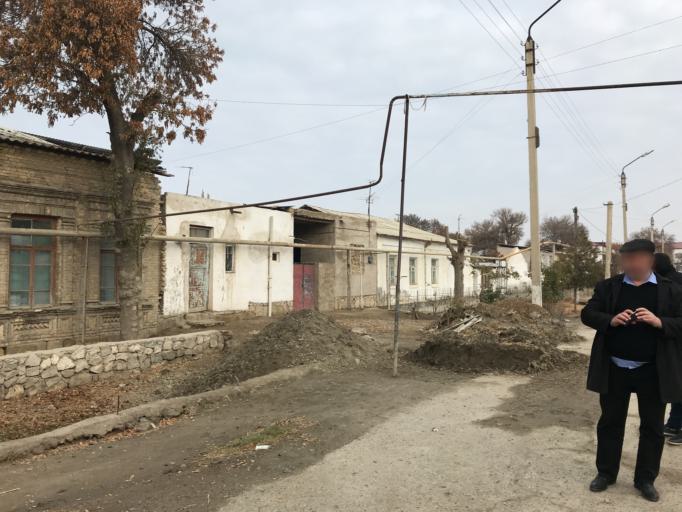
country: UZ
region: Bukhara
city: Kogon
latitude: 39.7217
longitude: 64.5540
